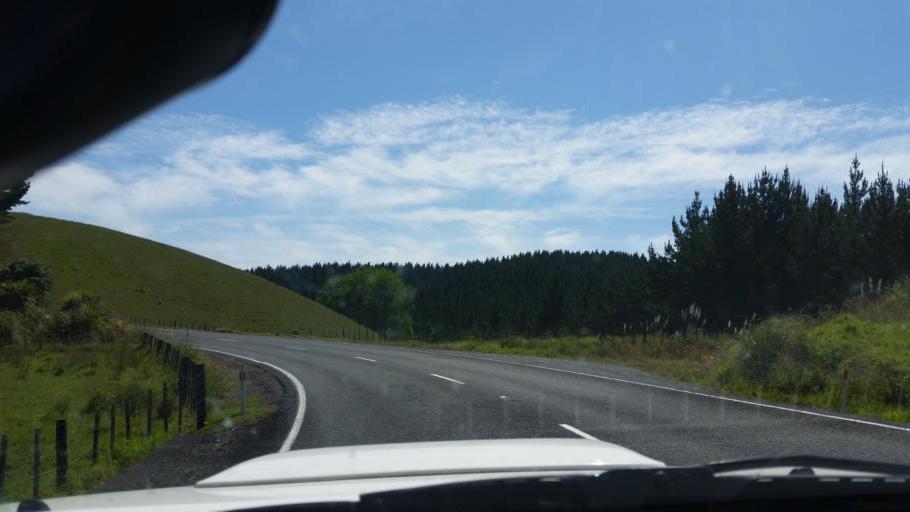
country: NZ
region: Auckland
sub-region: Auckland
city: Wellsford
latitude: -36.2032
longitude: 174.3962
